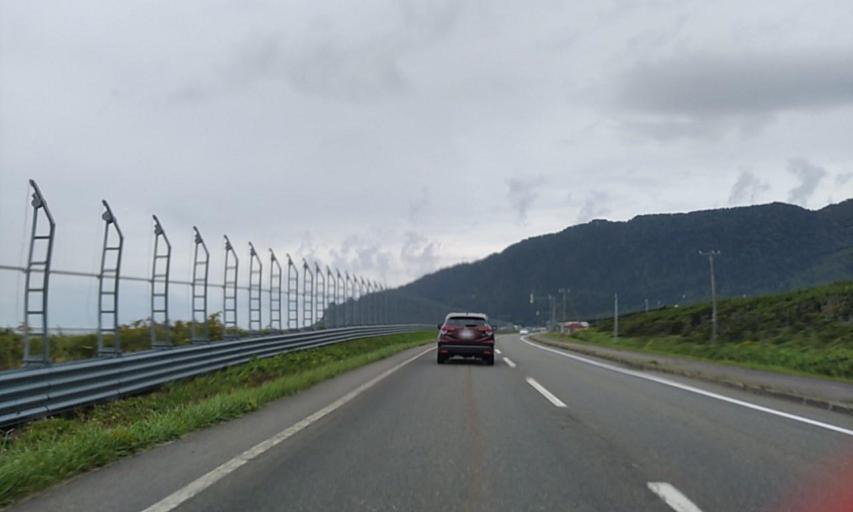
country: JP
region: Hokkaido
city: Makubetsu
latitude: 45.0734
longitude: 142.4659
